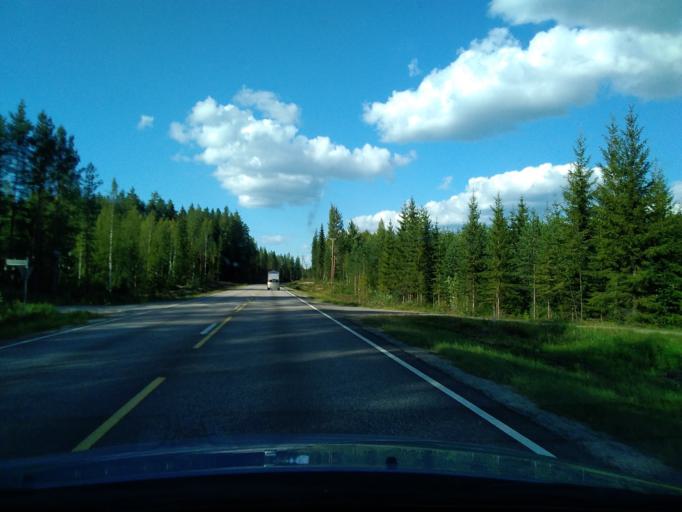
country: FI
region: Pirkanmaa
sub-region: Ylae-Pirkanmaa
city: Maenttae
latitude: 62.1075
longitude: 24.7386
